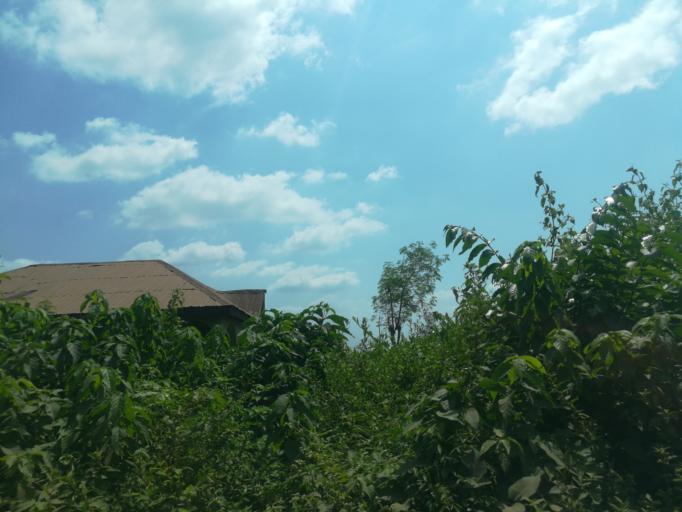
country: NG
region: Oyo
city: Moniya
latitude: 7.5420
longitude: 3.9097
